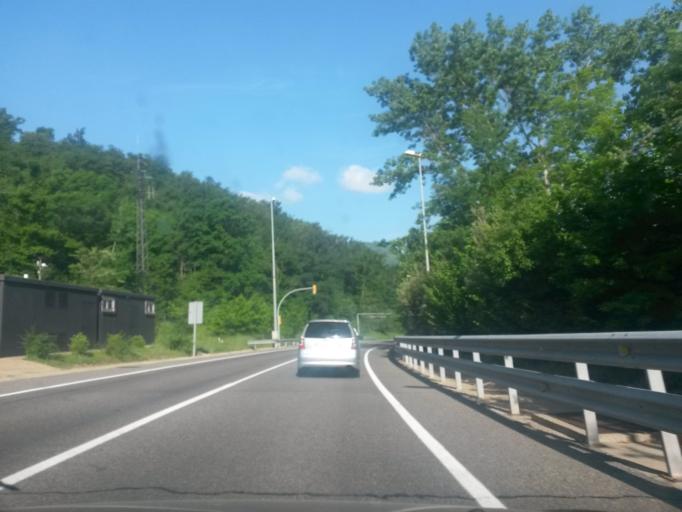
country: ES
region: Catalonia
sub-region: Provincia de Girona
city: Bas
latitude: 42.1249
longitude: 2.4551
